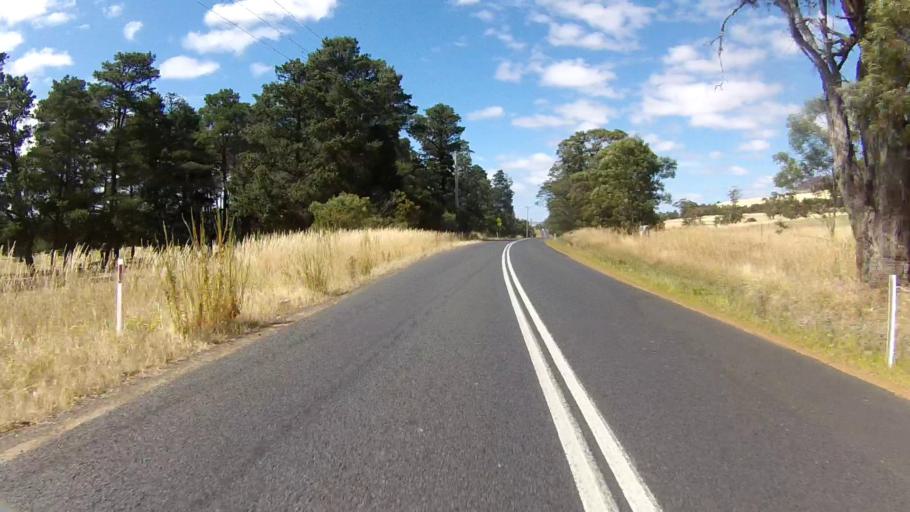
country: AU
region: Tasmania
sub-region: Sorell
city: Sorell
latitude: -42.6129
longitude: 147.4276
